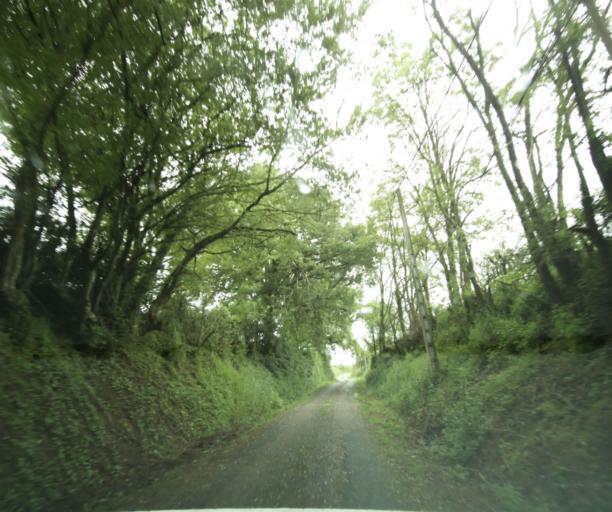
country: FR
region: Bourgogne
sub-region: Departement de Saone-et-Loire
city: Saint-Vallier
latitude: 46.4877
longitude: 4.4661
